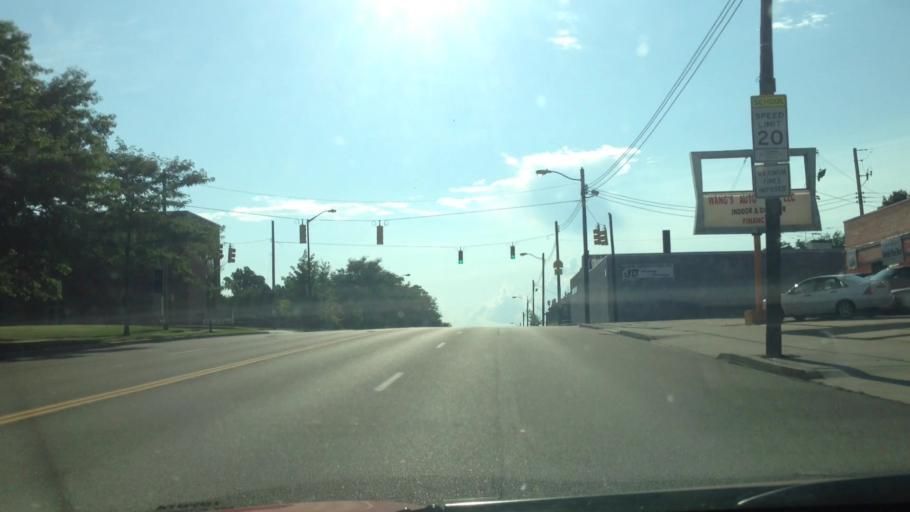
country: US
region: Ohio
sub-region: Summit County
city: Akron
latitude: 41.0712
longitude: -81.4966
